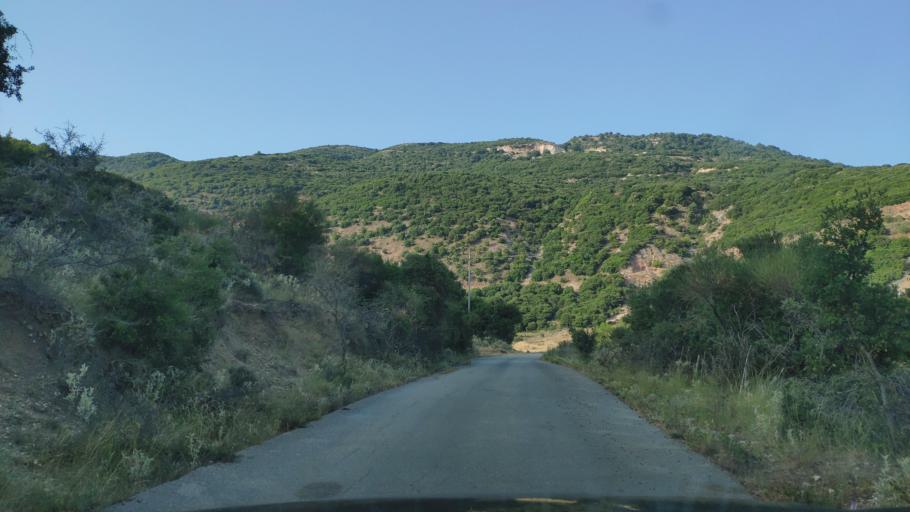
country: GR
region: West Greece
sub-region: Nomos Aitolias kai Akarnanias
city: Monastirakion
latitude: 38.8487
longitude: 20.9799
